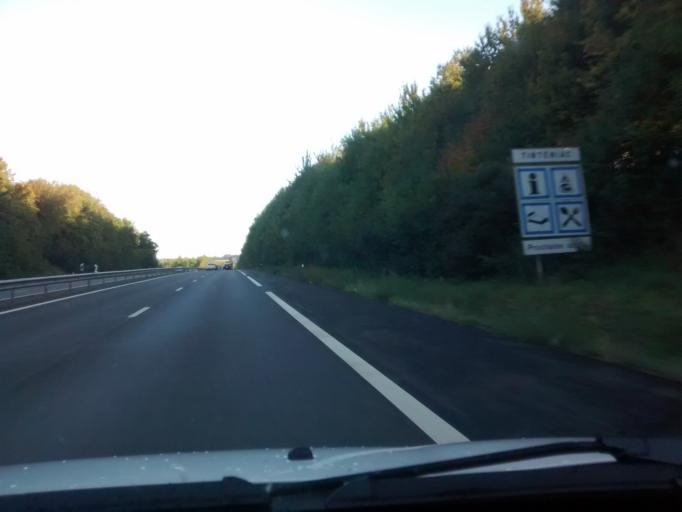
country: FR
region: Brittany
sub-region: Departement d'Ille-et-Vilaine
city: Tinteniac
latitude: 48.3198
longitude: -1.8464
